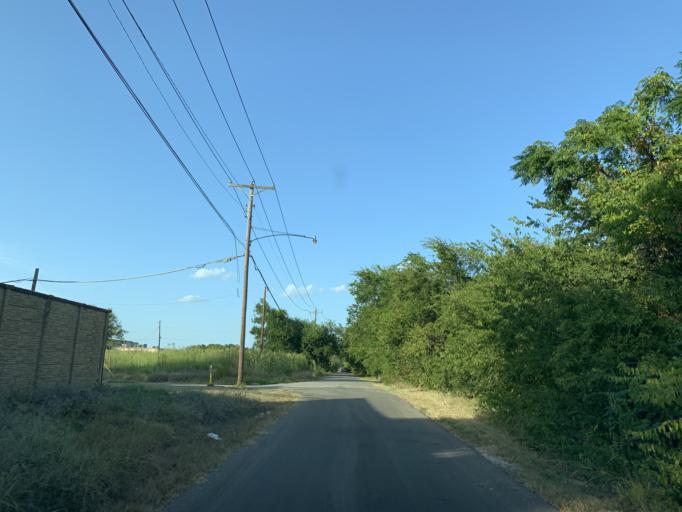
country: US
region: Texas
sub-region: Dallas County
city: Dallas
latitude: 32.7566
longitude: -96.7448
